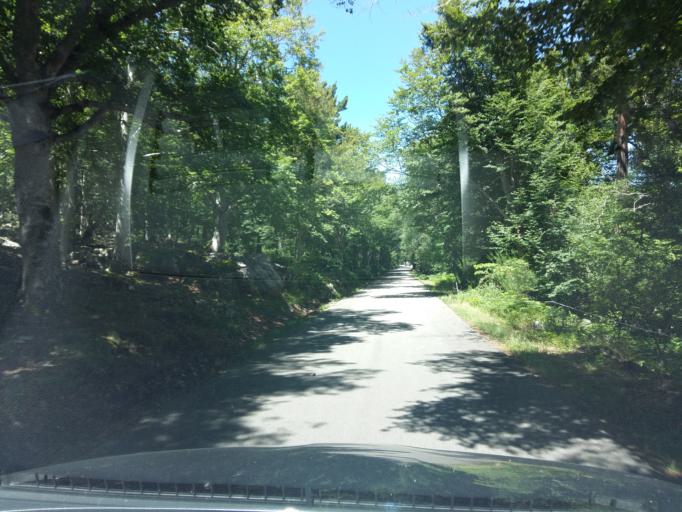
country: ES
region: Castille and Leon
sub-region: Provincia de Soria
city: Vozmediano
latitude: 41.8035
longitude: -1.8122
